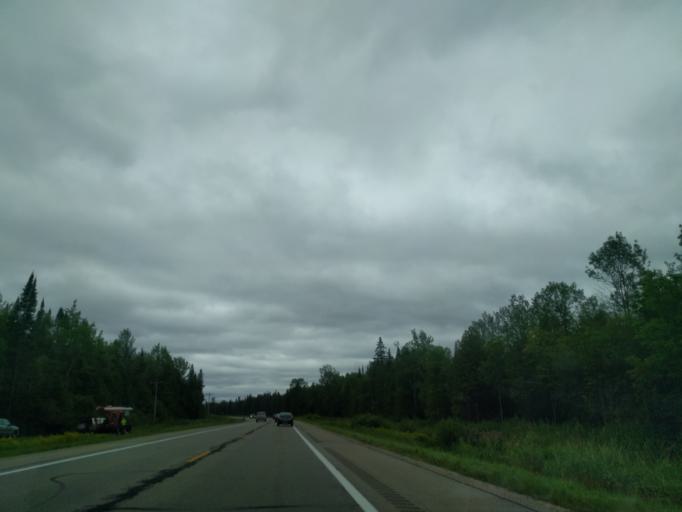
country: US
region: Michigan
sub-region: Delta County
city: Escanaba
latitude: 45.6501
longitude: -87.1832
